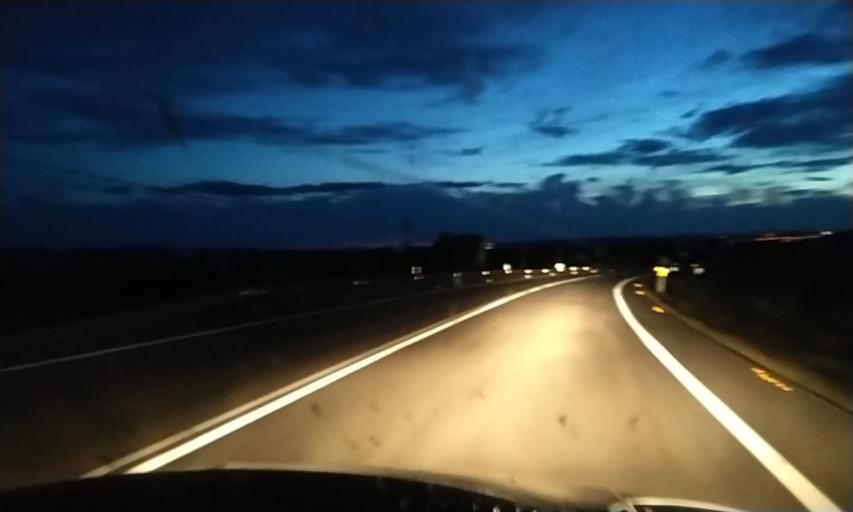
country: ES
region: Extremadura
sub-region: Provincia de Caceres
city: Galisteo
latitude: 39.9766
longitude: -6.2192
